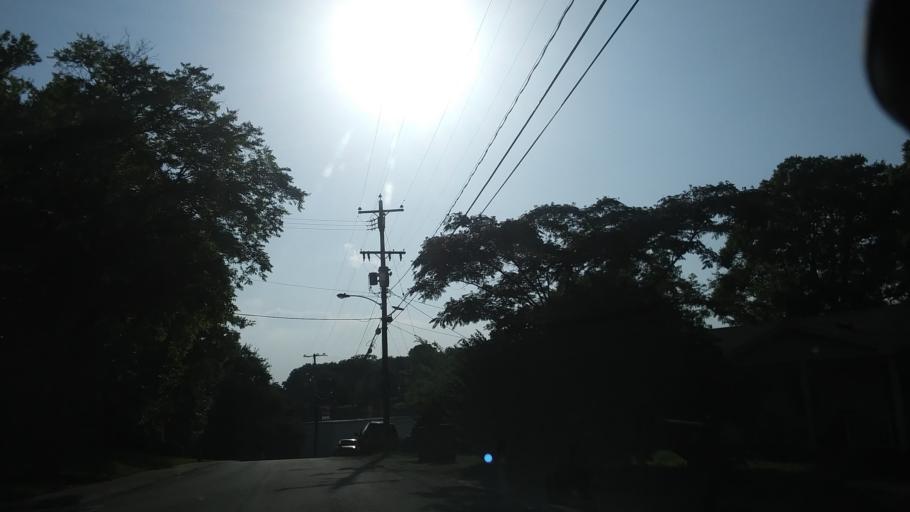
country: US
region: Tennessee
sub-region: Davidson County
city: Belle Meade
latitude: 36.1435
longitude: -86.8712
